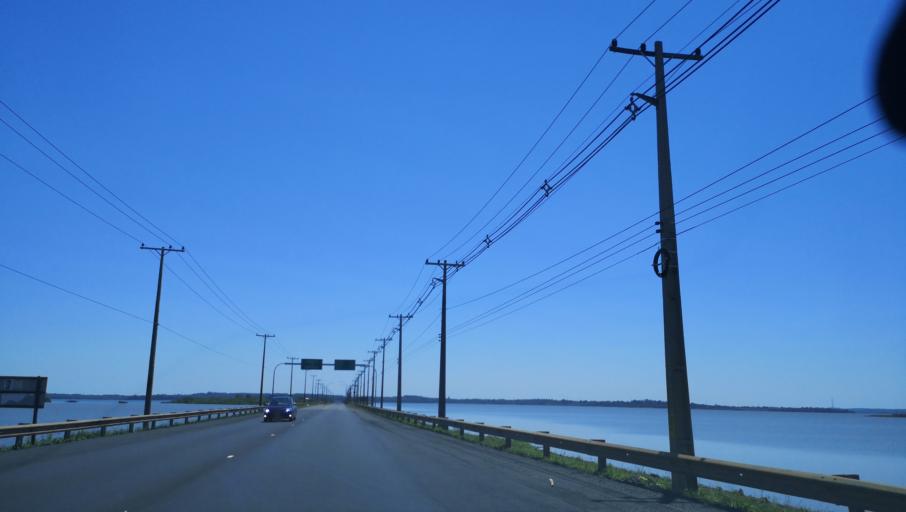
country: PY
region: Itapua
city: Carmen del Parana
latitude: -27.2148
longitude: -56.1511
